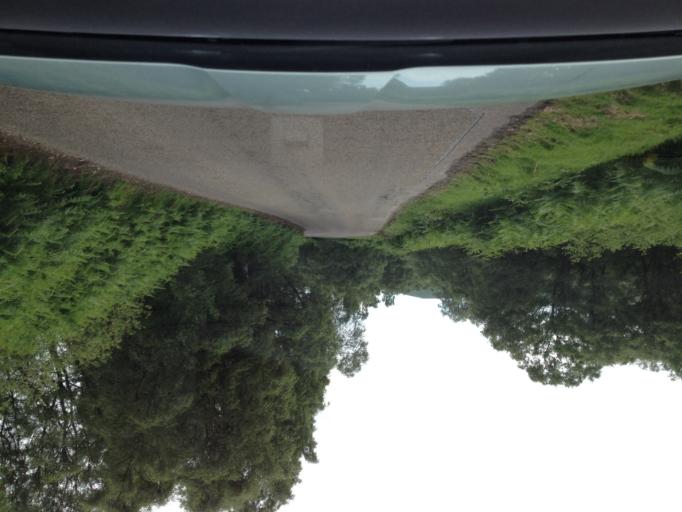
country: GB
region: Scotland
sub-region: Aberdeenshire
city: Aboyne
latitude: 56.8967
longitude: -2.7653
